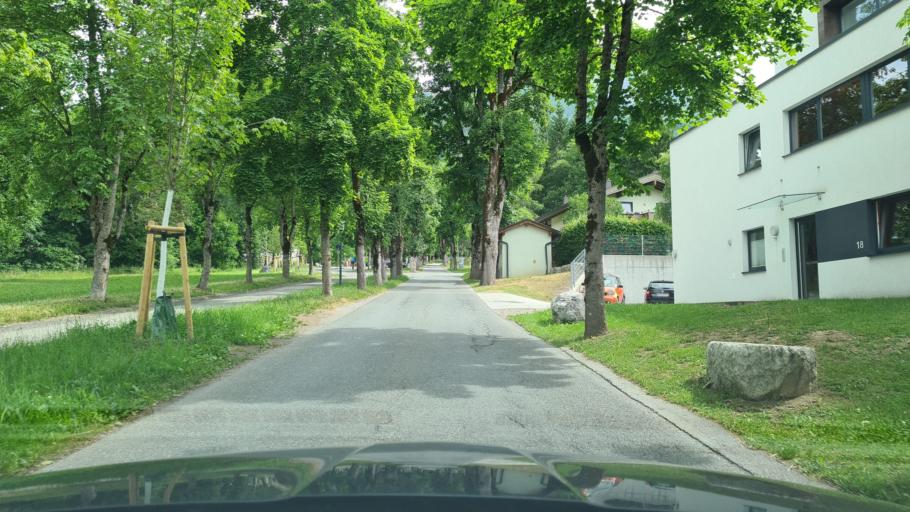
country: AT
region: Salzburg
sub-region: Politischer Bezirk Zell am See
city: Saalfelden am Steinernen Meer
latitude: 47.4364
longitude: 12.8571
